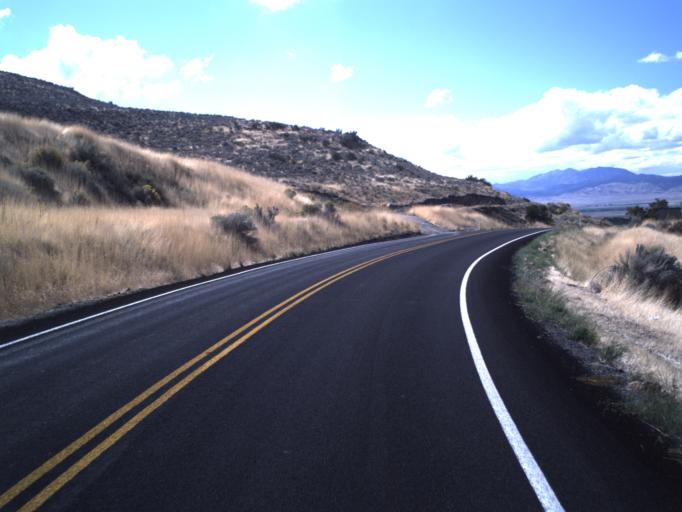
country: US
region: Utah
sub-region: Utah County
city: Genola
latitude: 40.0028
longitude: -111.8141
